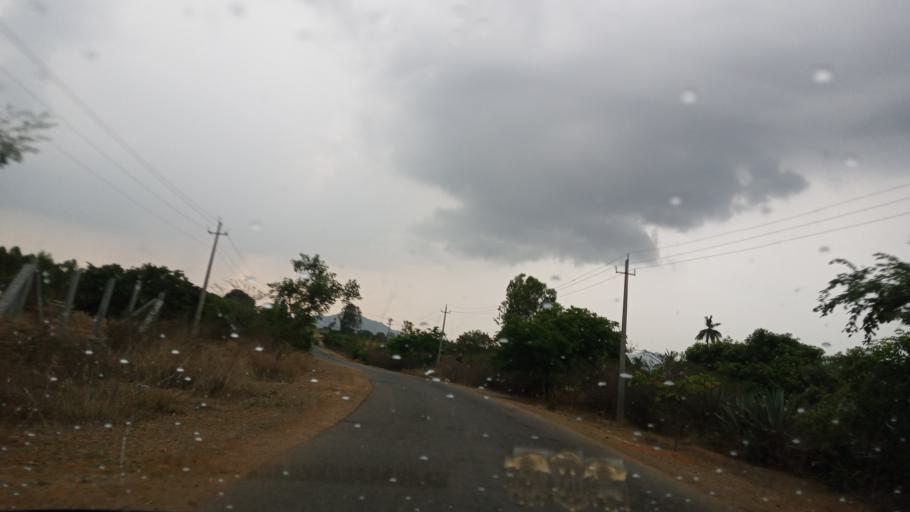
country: IN
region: Karnataka
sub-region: Kolar
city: Mulbagal
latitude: 13.1386
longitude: 78.3622
